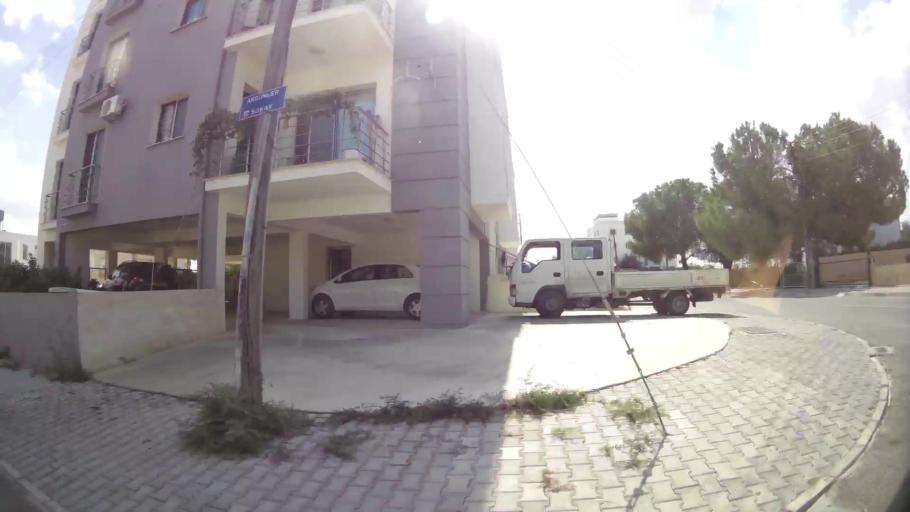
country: CY
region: Lefkosia
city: Nicosia
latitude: 35.2164
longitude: 33.2949
